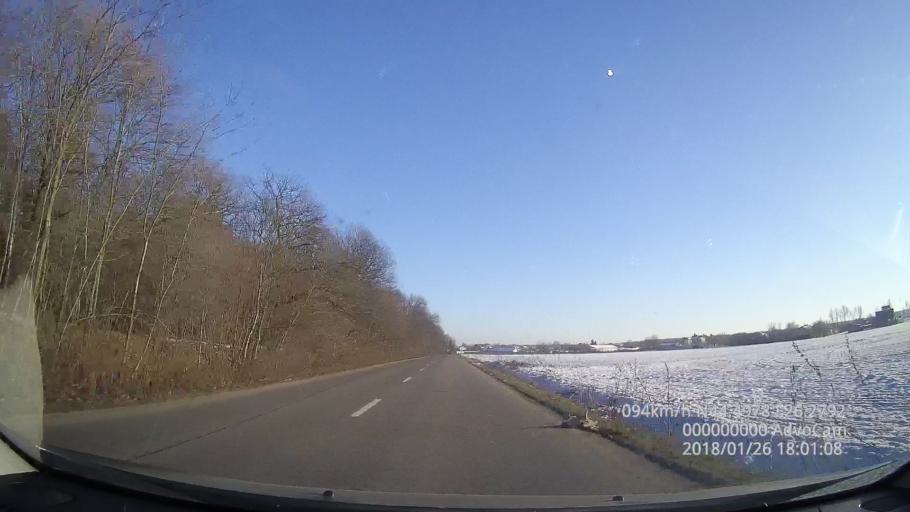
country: RO
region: Ilfov
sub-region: Comuna Ganeasa
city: Ganeasa
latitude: 44.4972
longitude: 26.2798
